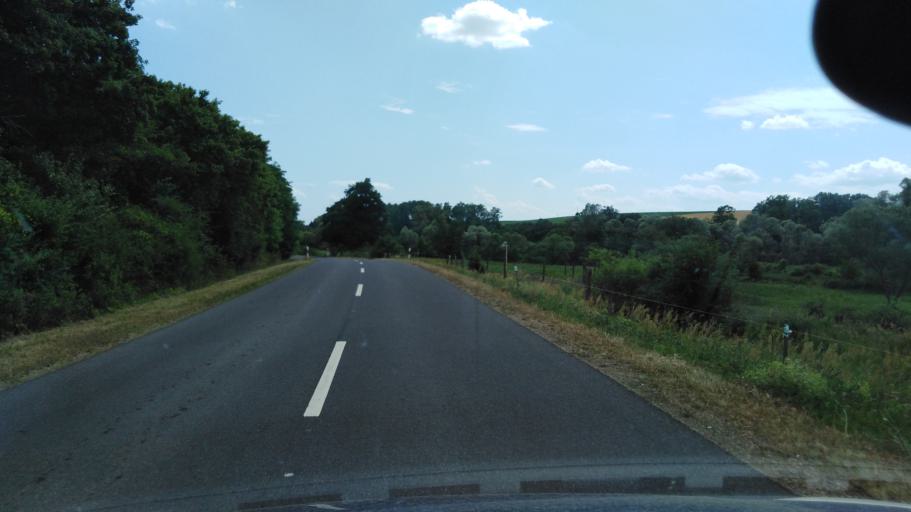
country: HU
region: Nograd
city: Szecseny
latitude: 48.2021
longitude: 19.5268
